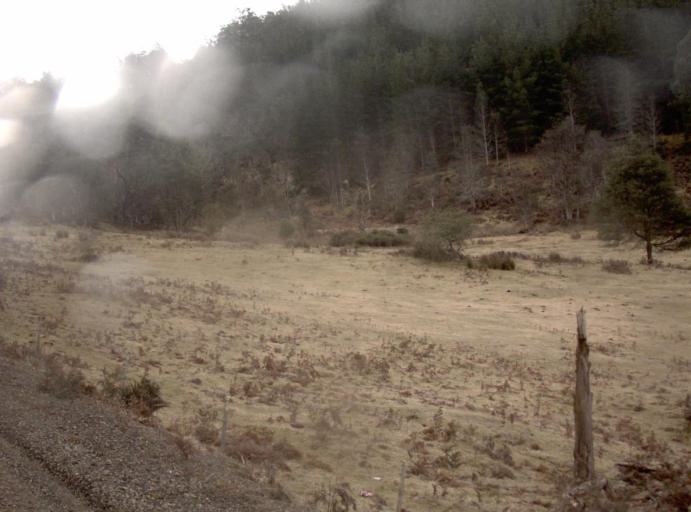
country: AU
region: Tasmania
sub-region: Dorset
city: Scottsdale
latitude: -41.3037
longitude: 147.3670
